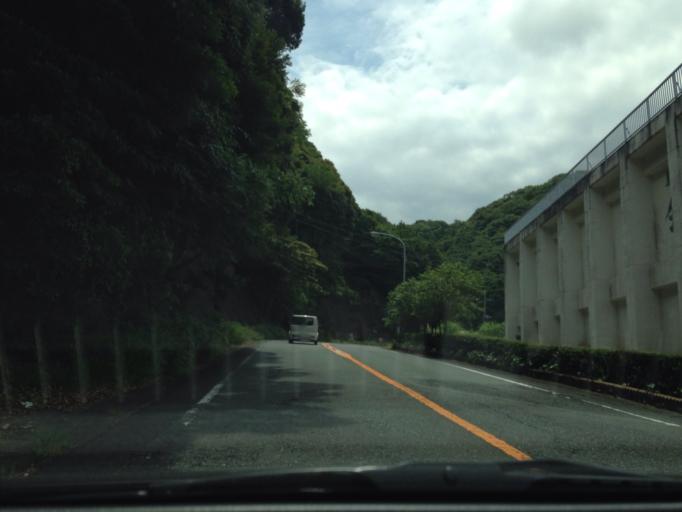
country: JP
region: Shizuoka
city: Heda
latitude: 34.8086
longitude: 138.7757
